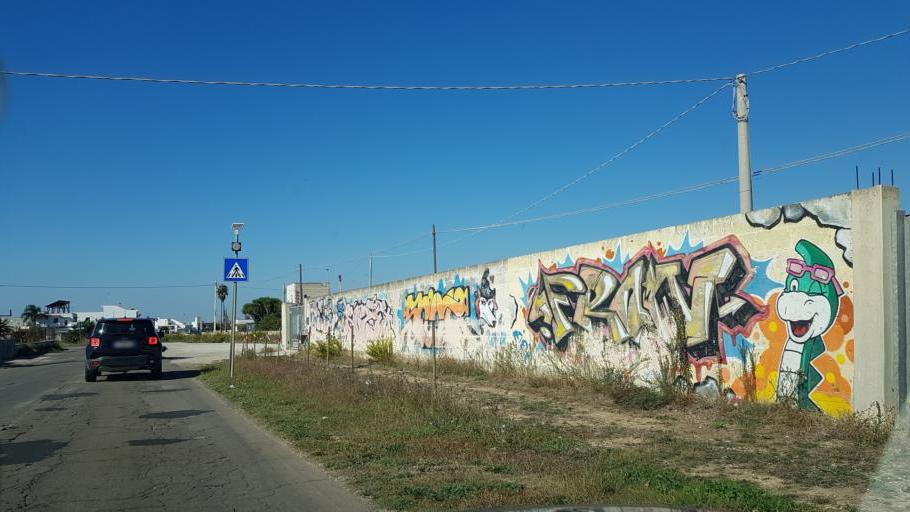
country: IT
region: Apulia
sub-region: Provincia di Lecce
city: Leverano
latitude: 40.2979
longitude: 18.0006
